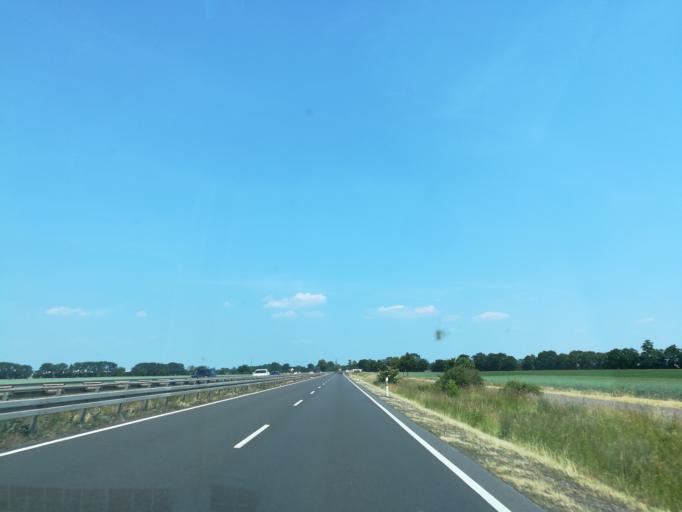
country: DE
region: Saxony-Anhalt
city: Wolmirsleben
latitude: 52.0201
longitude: 11.5116
